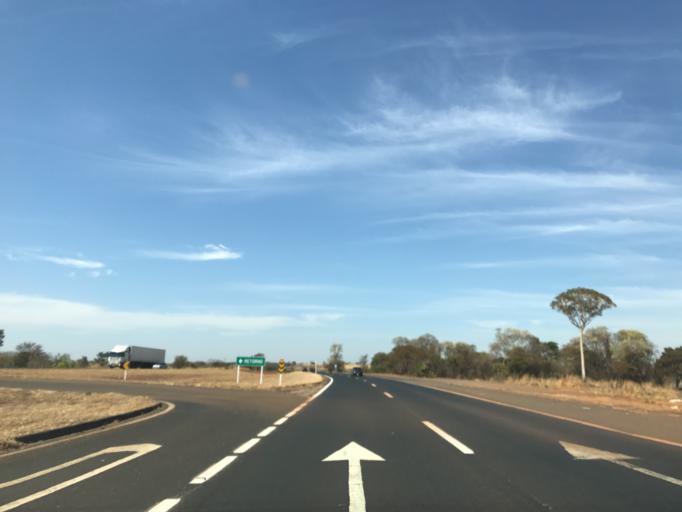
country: BR
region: Minas Gerais
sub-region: Monte Alegre De Minas
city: Monte Alegre de Minas
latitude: -18.8178
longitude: -49.0875
